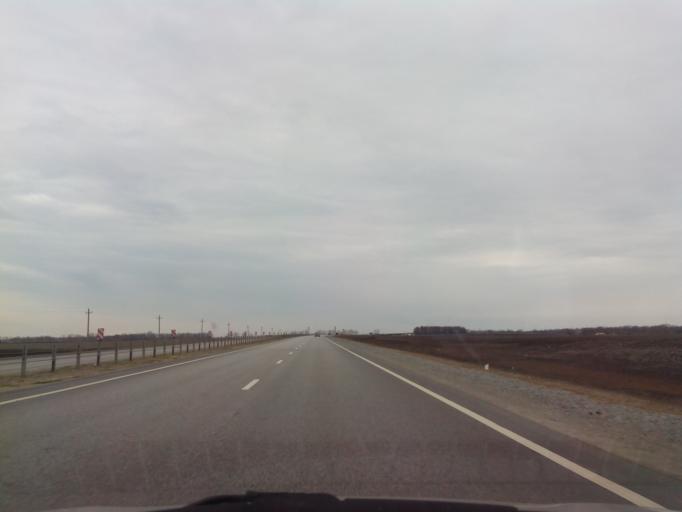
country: RU
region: Tambov
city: Zavoronezhskoye
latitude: 52.9043
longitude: 40.6485
